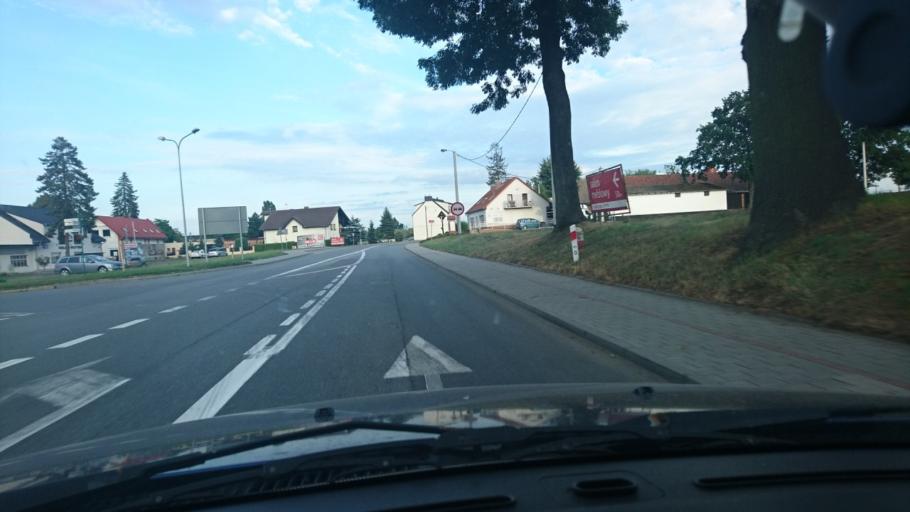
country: PL
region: Opole Voivodeship
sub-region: Powiat oleski
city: Olesno
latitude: 50.8739
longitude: 18.4256
